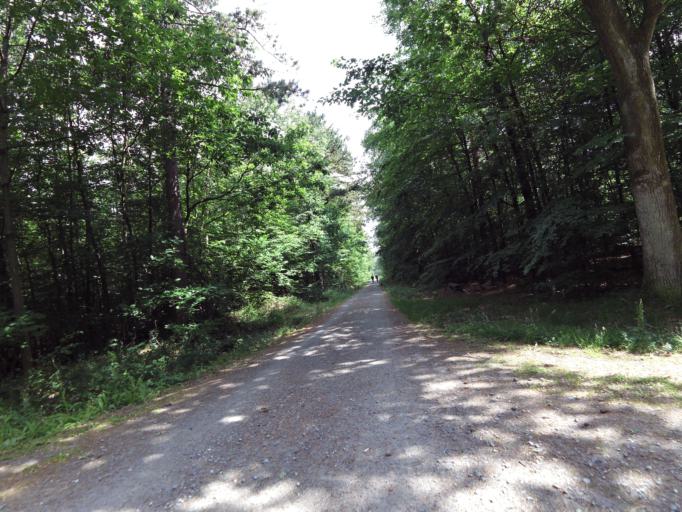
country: DE
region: Lower Saxony
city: Nordholz
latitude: 53.8484
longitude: 8.5947
